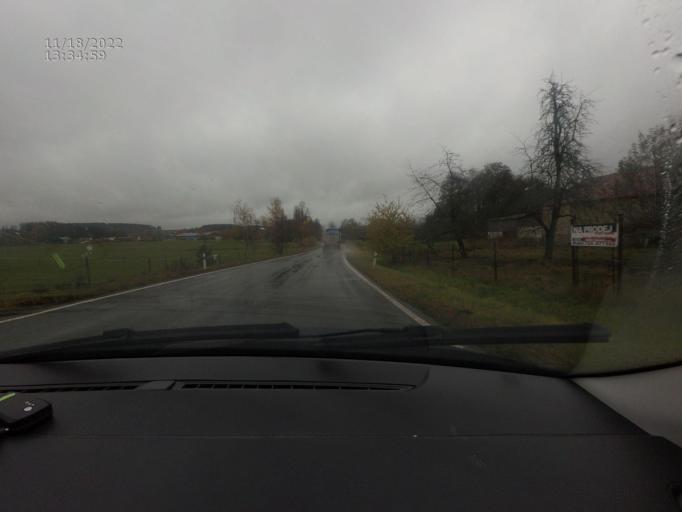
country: CZ
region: Plzensky
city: Kasejovice
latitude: 49.4051
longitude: 13.7764
